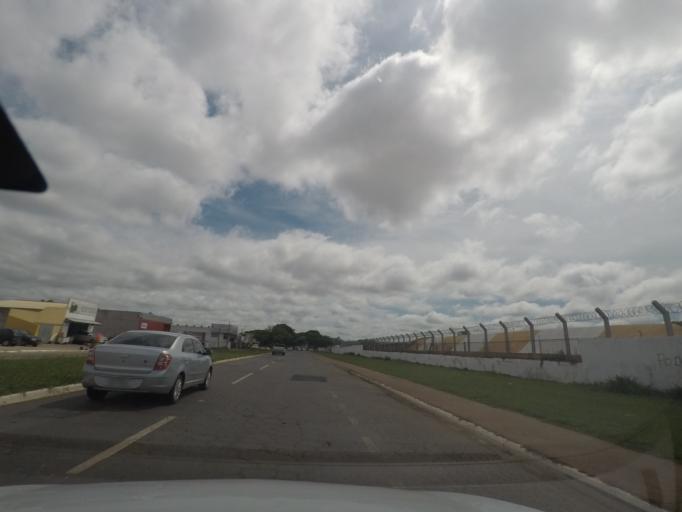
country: BR
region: Goias
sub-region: Goiania
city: Goiania
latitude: -16.6263
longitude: -49.2321
